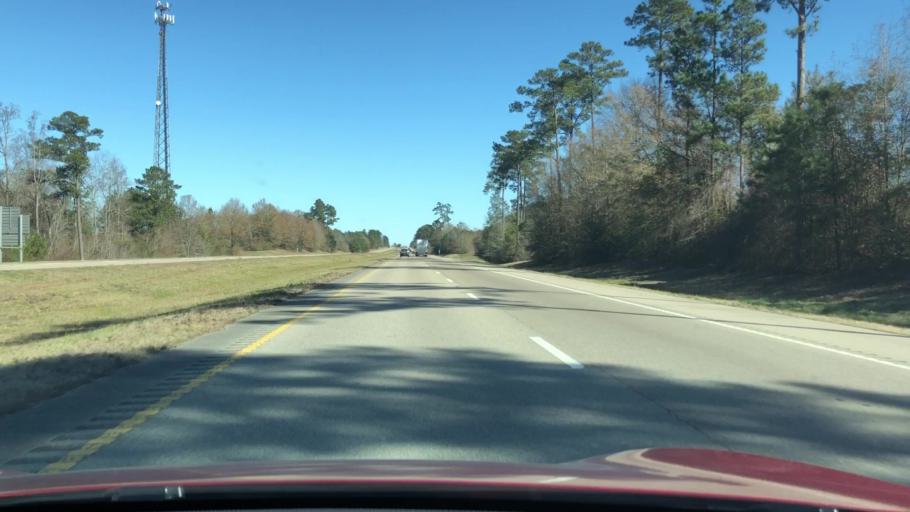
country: US
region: Mississippi
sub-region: Pearl River County
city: Poplarville
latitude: 30.7315
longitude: -89.5445
